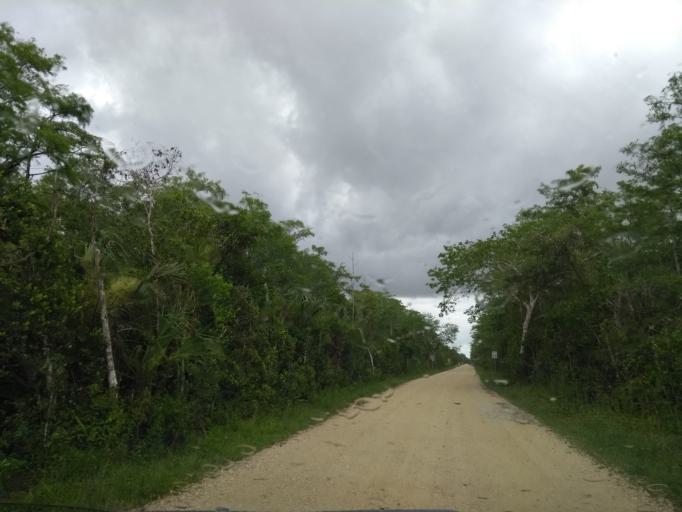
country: US
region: Florida
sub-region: Miami-Dade County
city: The Hammocks
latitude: 25.7468
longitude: -80.9546
